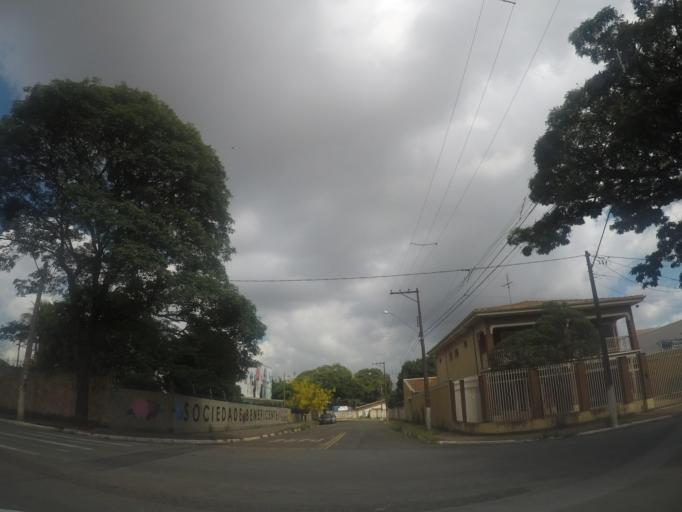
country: BR
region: Sao Paulo
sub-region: Hortolandia
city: Hortolandia
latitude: -22.8542
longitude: -47.1645
